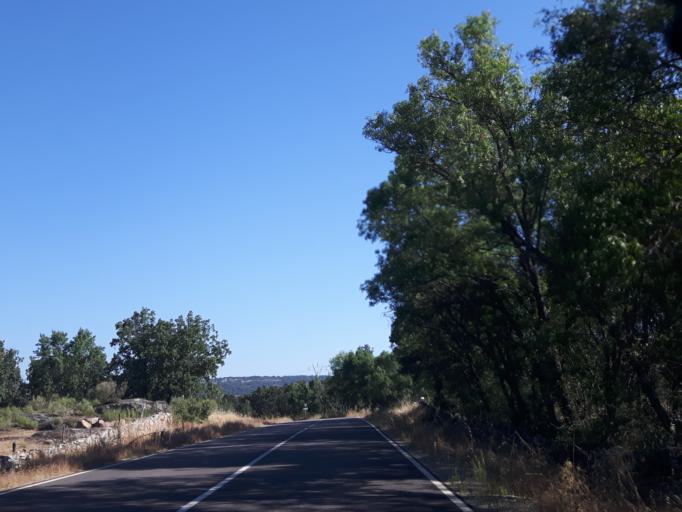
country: ES
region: Castille and Leon
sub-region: Provincia de Salamanca
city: Valdehijaderos
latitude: 40.4279
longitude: -5.8221
